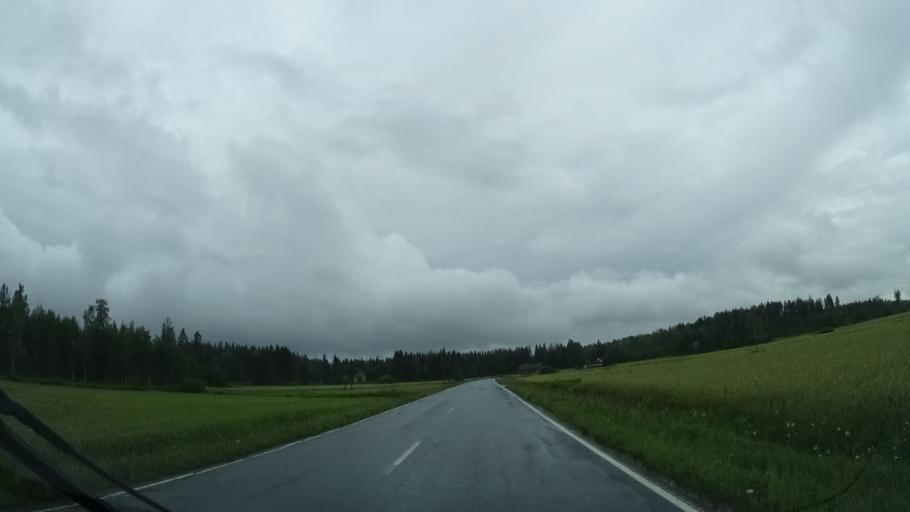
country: FI
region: Haeme
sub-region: Forssa
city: Humppila
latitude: 60.9853
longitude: 23.2536
